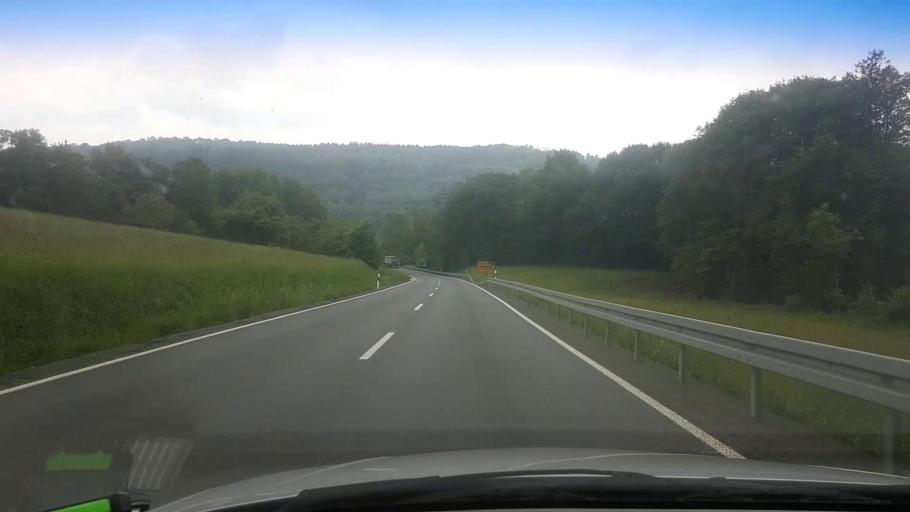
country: DE
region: Bavaria
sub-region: Upper Franconia
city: Reuth
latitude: 49.9722
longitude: 11.6914
